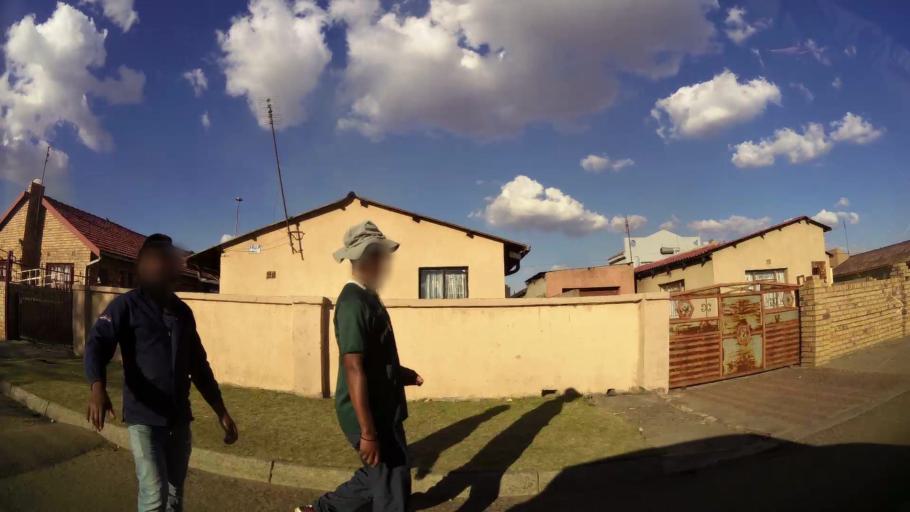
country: ZA
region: Mpumalanga
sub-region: Nkangala District Municipality
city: Witbank
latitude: -25.8677
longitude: 29.1714
